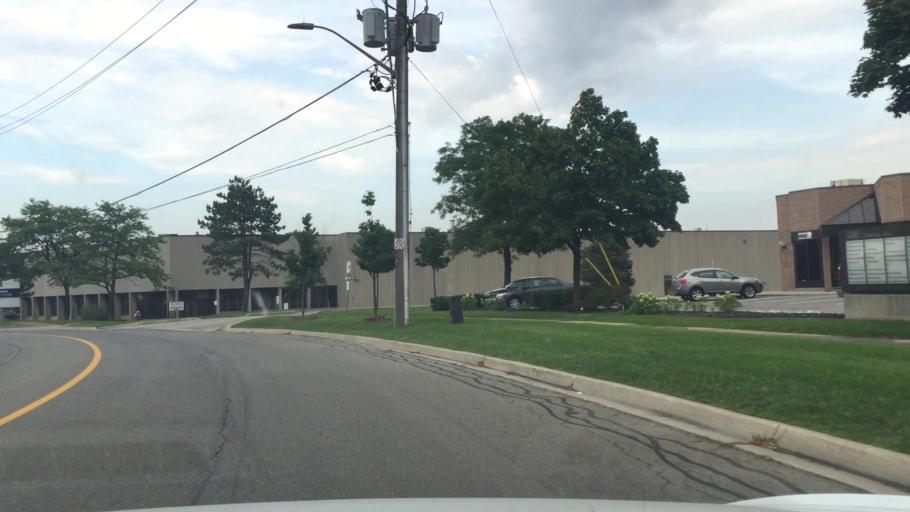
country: CA
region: Ontario
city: Mississauga
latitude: 43.6256
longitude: -79.6365
